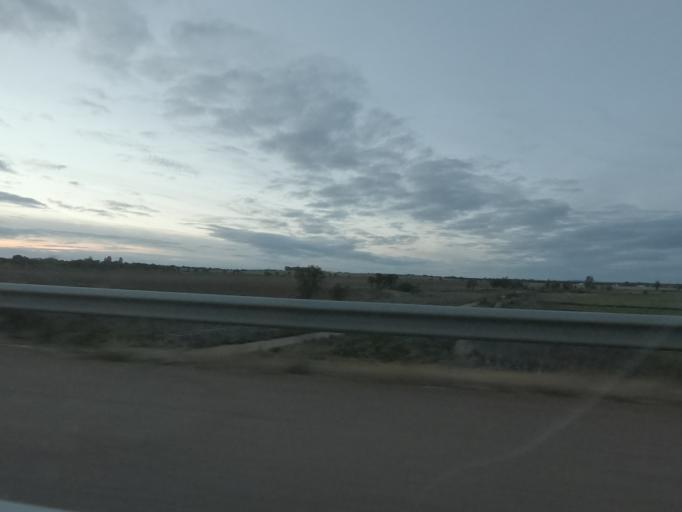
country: ES
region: Extremadura
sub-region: Provincia de Badajoz
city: Badajoz
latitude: 38.9198
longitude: -6.9704
